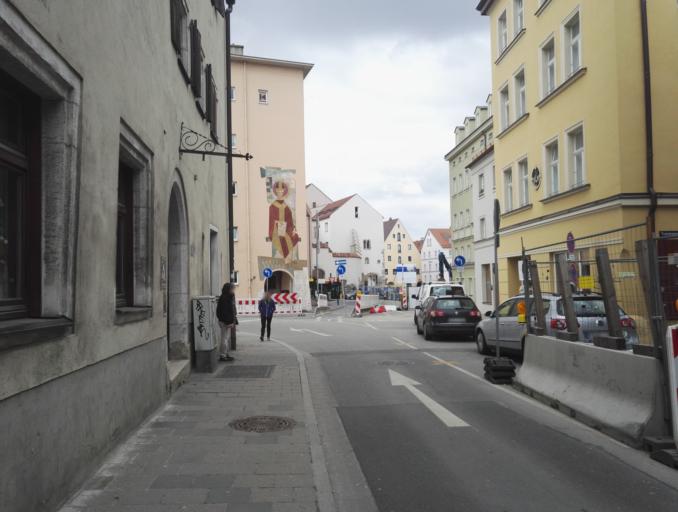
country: DE
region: Bavaria
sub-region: Upper Palatinate
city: Regensburg
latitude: 49.0194
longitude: 12.1028
